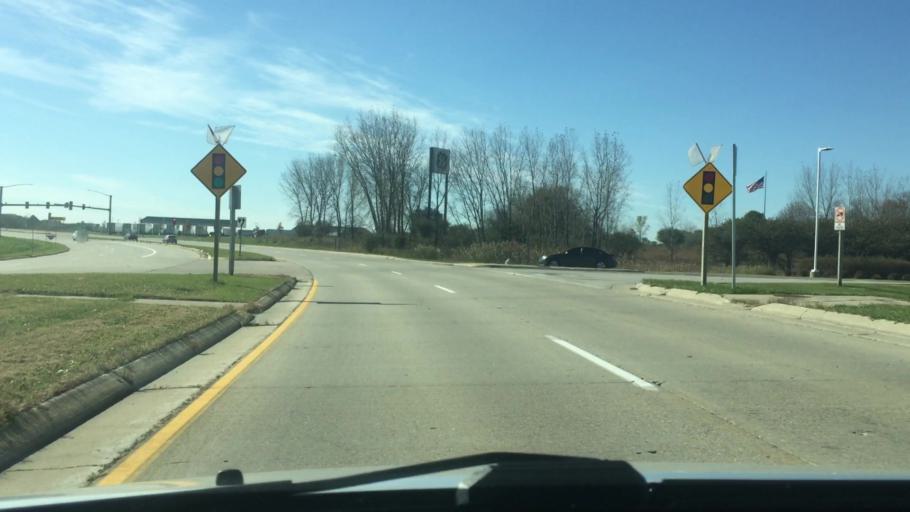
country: US
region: Wisconsin
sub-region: Waukesha County
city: Pewaukee
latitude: 43.0510
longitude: -88.2545
